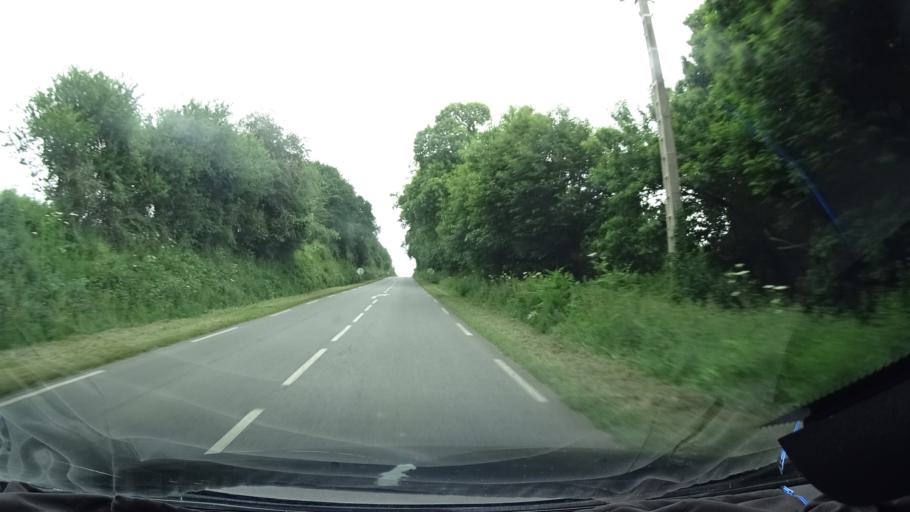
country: FR
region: Brittany
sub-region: Departement d'Ille-et-Vilaine
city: La Richardais
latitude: 48.5996
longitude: -2.0356
